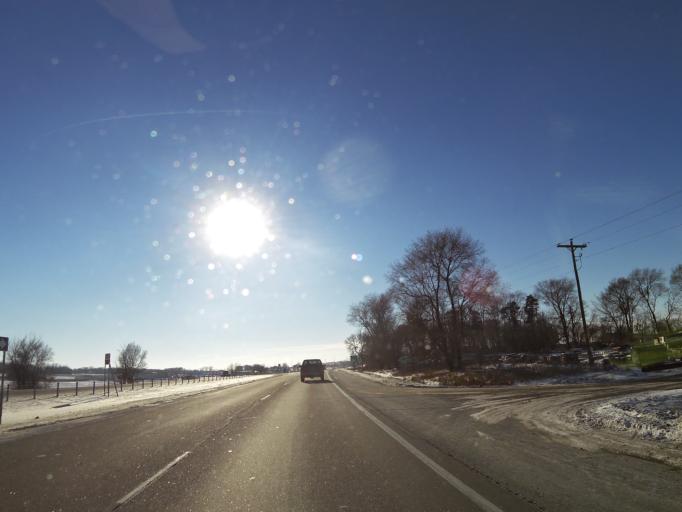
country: US
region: Minnesota
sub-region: Carver County
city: Chaska
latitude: 44.7723
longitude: -93.5702
